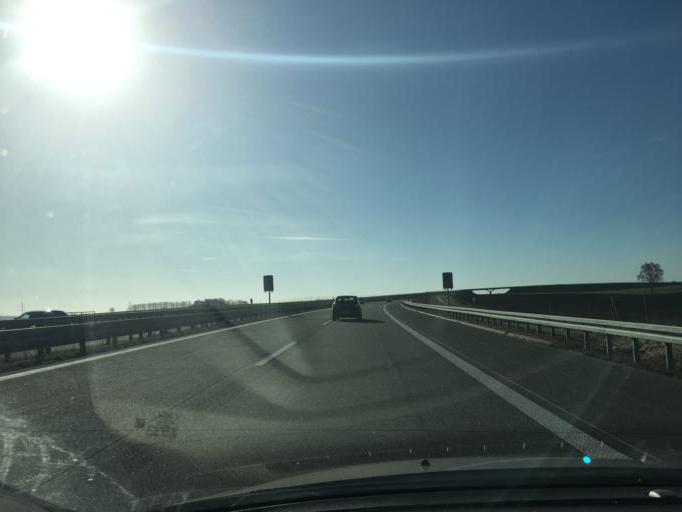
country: DE
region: Saxony
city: Geithain
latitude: 51.0408
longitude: 12.6793
